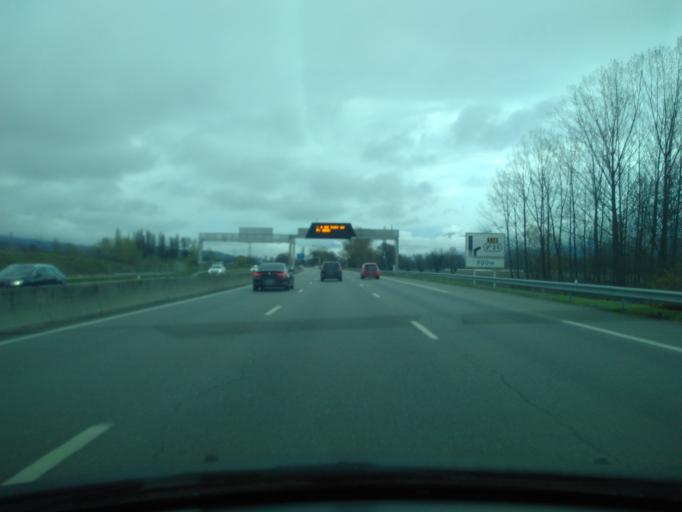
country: FR
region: Rhone-Alpes
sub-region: Departement de l'Isere
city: Montbonnot-Saint-Martin
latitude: 45.2116
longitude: 5.8090
